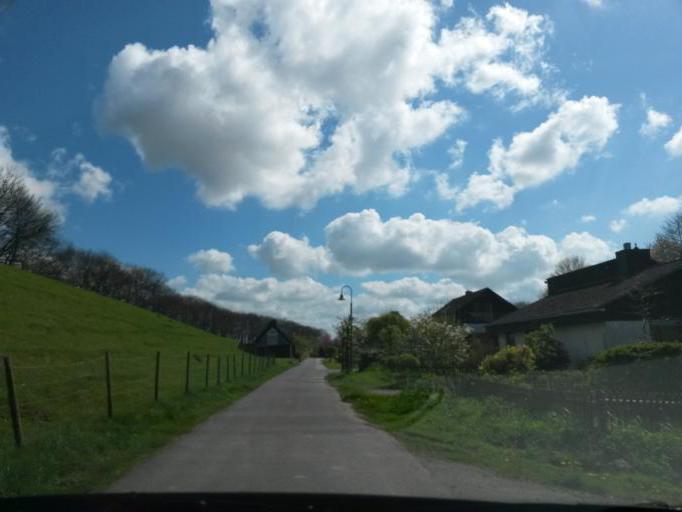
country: DE
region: Schleswig-Holstein
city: Seestermuhe
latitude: 53.6643
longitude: 9.5574
